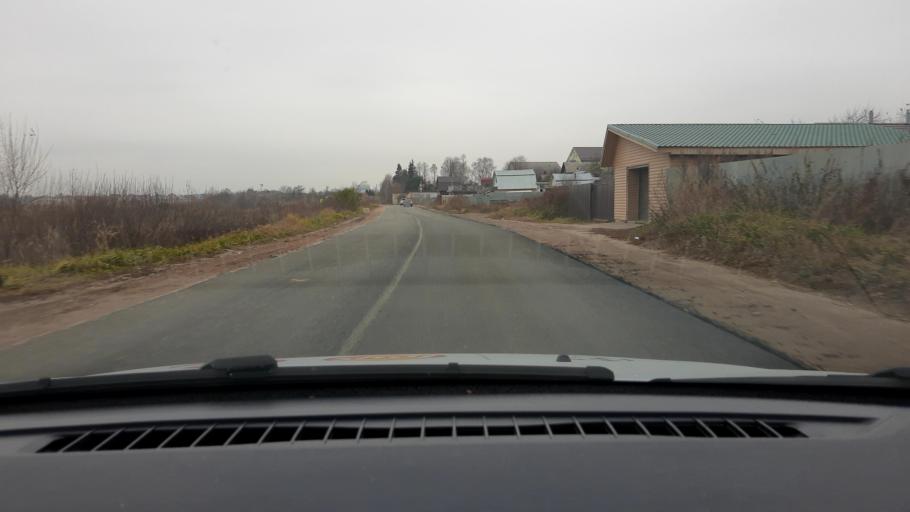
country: RU
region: Nizjnij Novgorod
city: Neklyudovo
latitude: 56.4181
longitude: 43.9682
